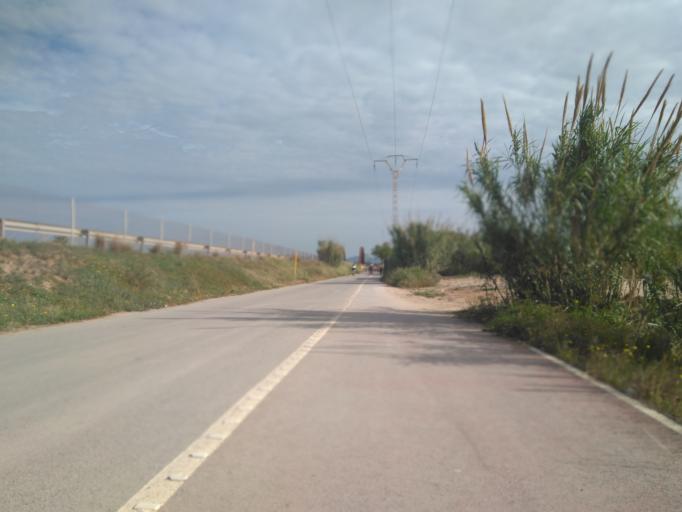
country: ES
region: Valencia
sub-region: Provincia de Valencia
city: Alboraya
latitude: 39.4997
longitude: -0.3254
